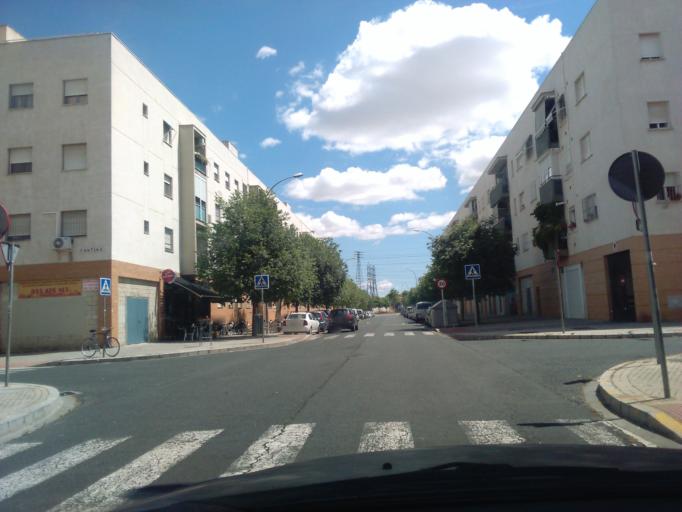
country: ES
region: Andalusia
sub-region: Provincia de Sevilla
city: Sevilla
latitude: 37.4197
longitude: -5.9855
